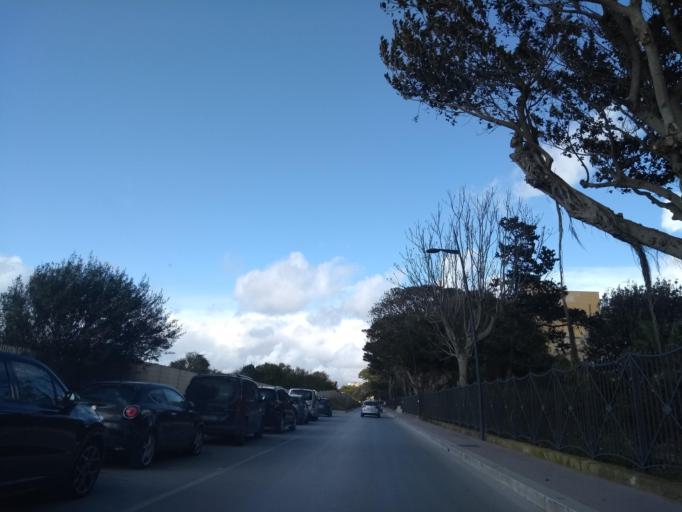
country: IT
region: Sicily
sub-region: Trapani
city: Marsala
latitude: 37.8020
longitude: 12.4319
